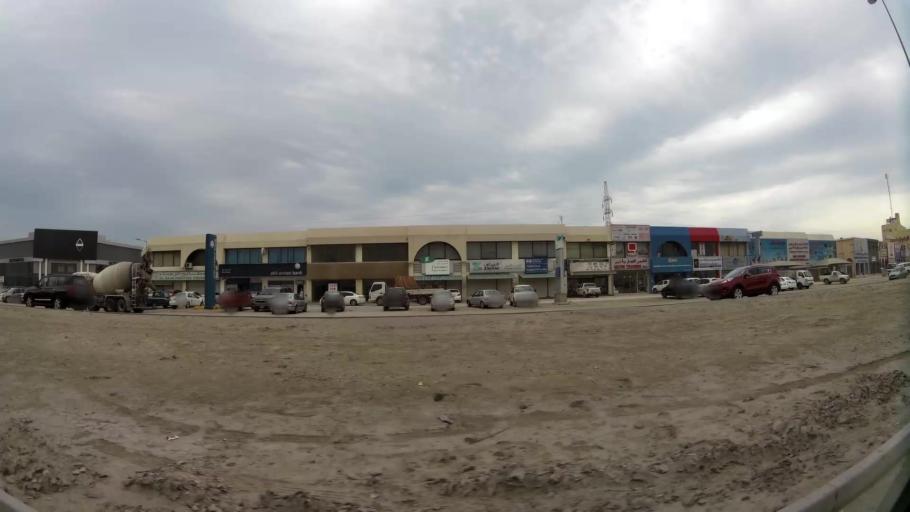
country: BH
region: Northern
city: Sitrah
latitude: 26.1574
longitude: 50.6067
